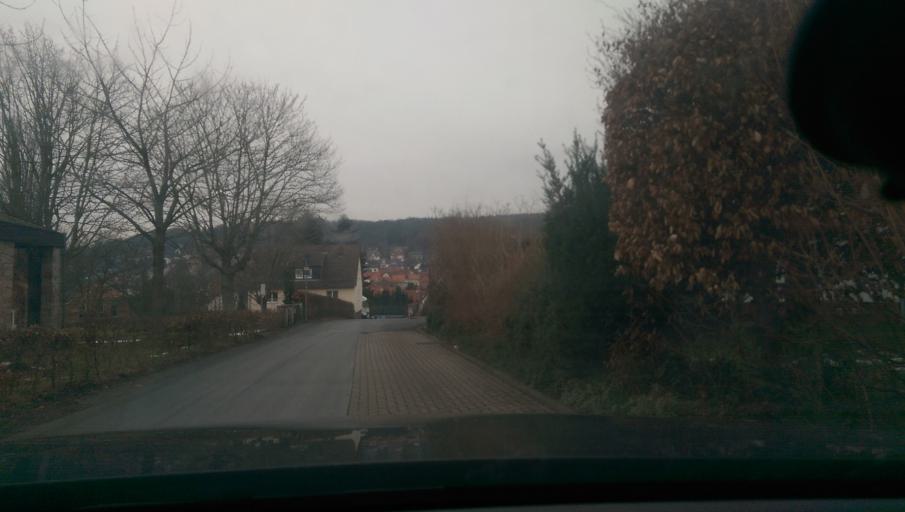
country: DE
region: Hesse
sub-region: Regierungsbezirk Kassel
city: Nieste
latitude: 51.3102
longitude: 9.6678
